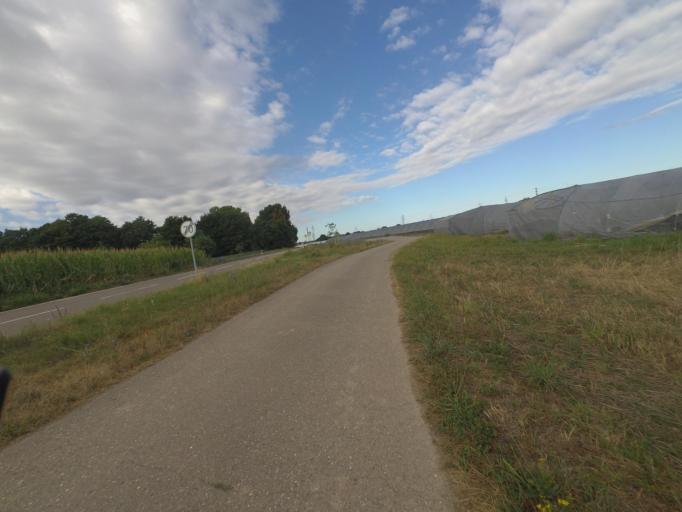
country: DE
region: Baden-Wuerttemberg
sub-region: Karlsruhe Region
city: Ottenhofen
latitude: 48.7494
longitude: 8.1489
